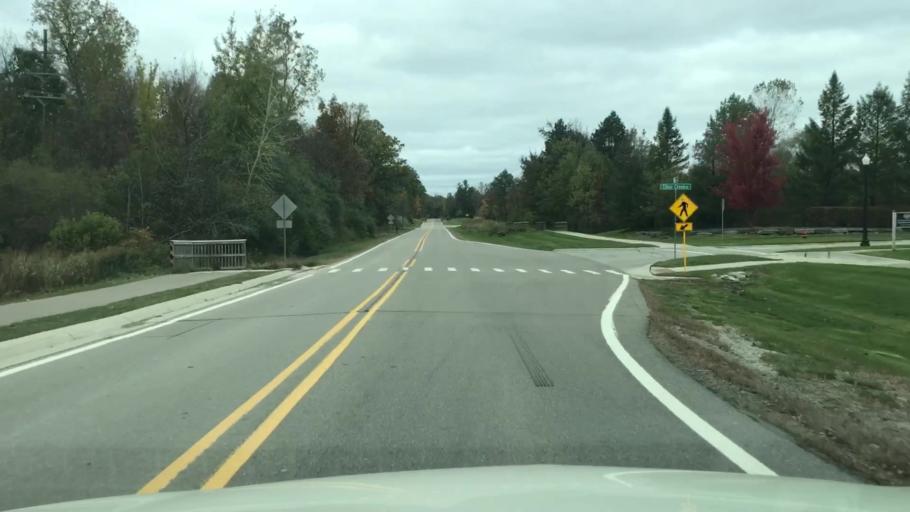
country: US
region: Michigan
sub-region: Oakland County
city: Rochester
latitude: 42.7048
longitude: -83.1243
